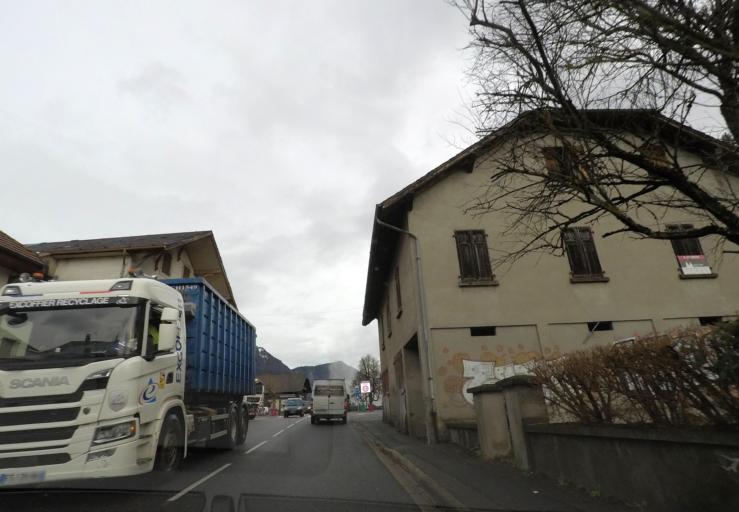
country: FR
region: Rhone-Alpes
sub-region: Departement de la Haute-Savoie
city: Chatillon-sur-Cluses
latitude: 46.0870
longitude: 6.5827
